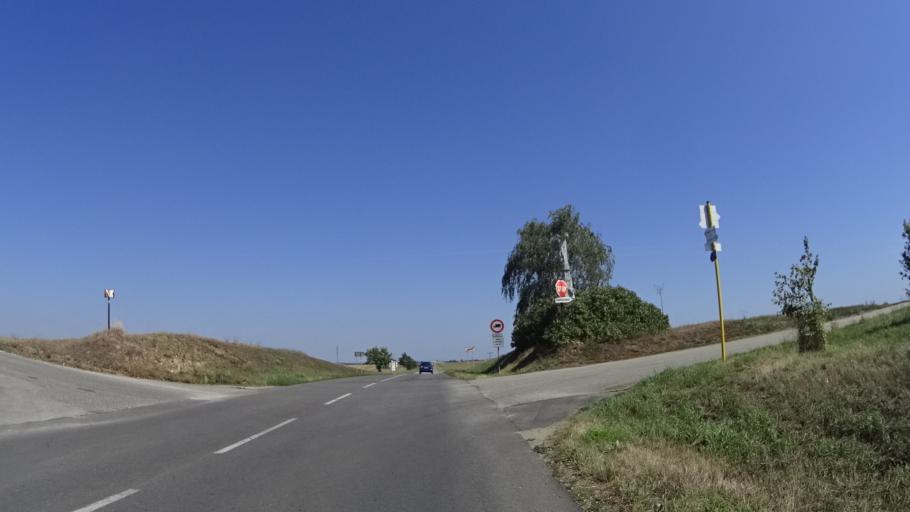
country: SK
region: Trnavsky
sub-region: Okres Skalica
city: Skalica
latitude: 48.8521
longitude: 17.2396
